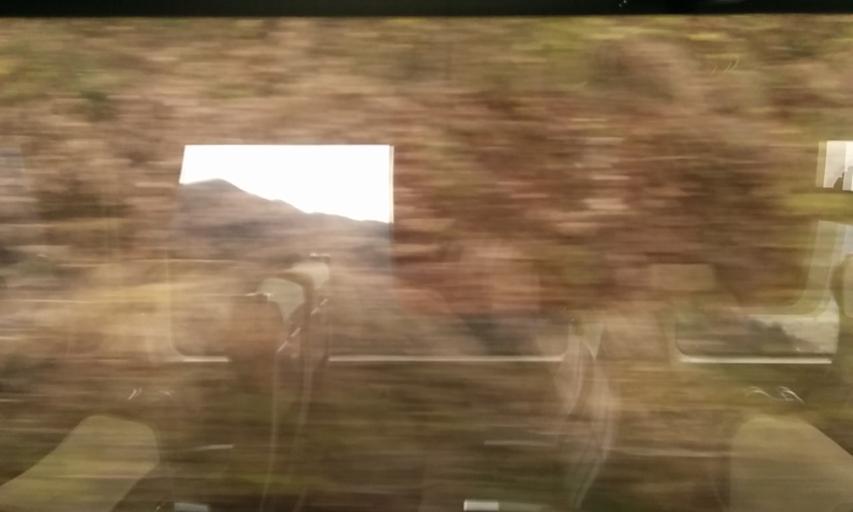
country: JP
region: Nagano
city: Nagano-shi
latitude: 36.4890
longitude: 138.1017
